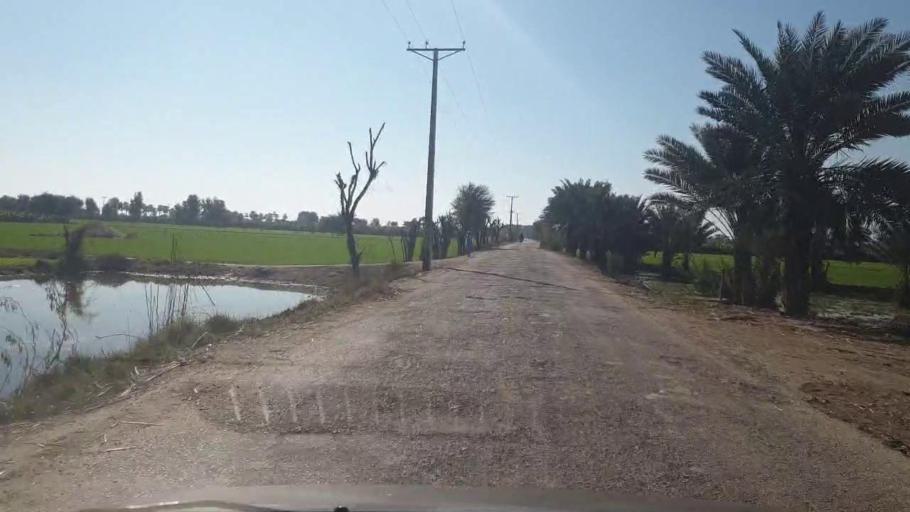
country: PK
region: Sindh
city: Bozdar
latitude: 27.2556
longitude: 68.6524
